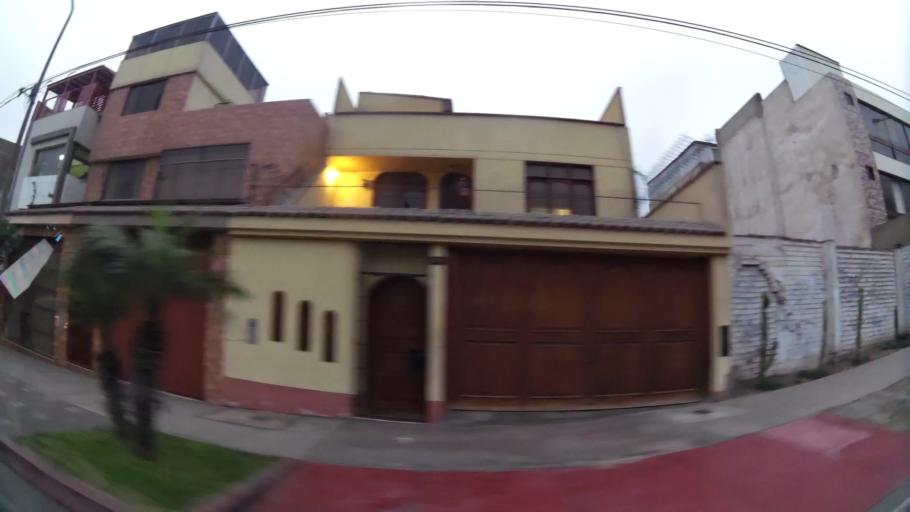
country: PE
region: Lima
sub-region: Lima
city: La Molina
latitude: -12.1049
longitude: -76.9474
